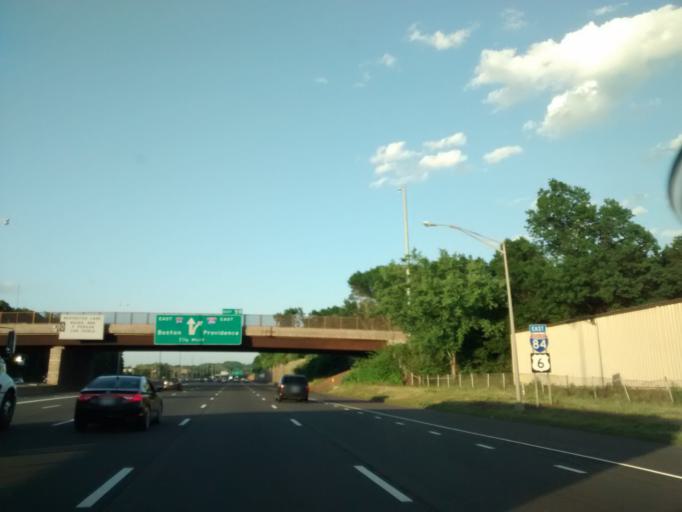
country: US
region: Connecticut
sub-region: Hartford County
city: East Hartford
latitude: 41.7671
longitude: -72.6195
